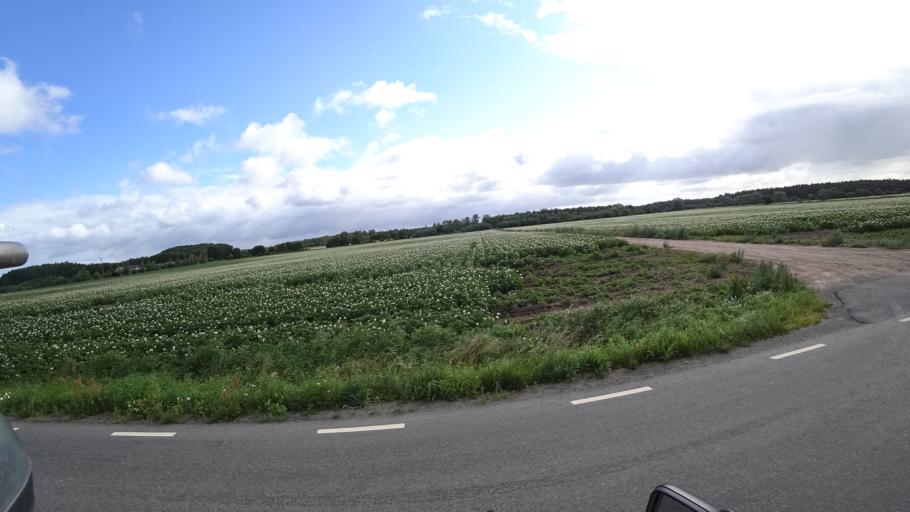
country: SE
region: Skane
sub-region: Kristianstads Kommun
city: Norra Asum
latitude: 55.9693
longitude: 14.1128
